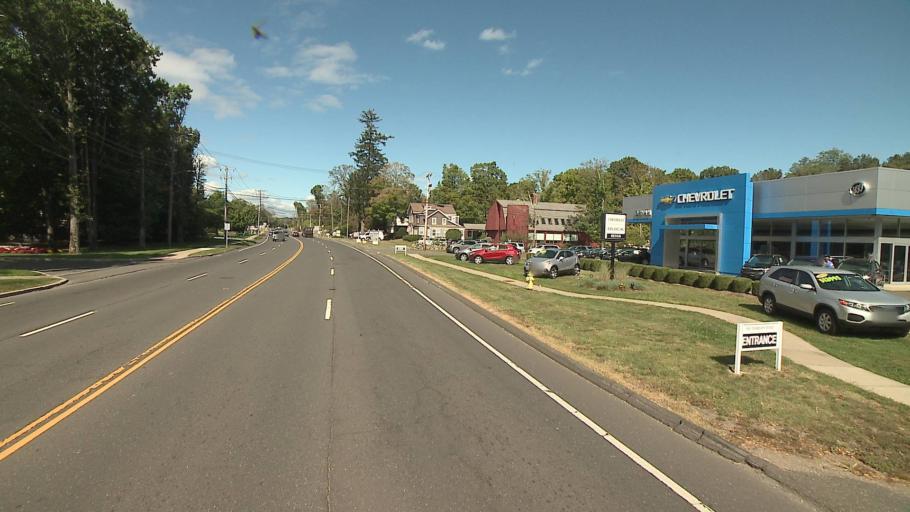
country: US
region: Connecticut
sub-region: Fairfield County
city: Wilton
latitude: 41.1849
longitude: -73.4203
